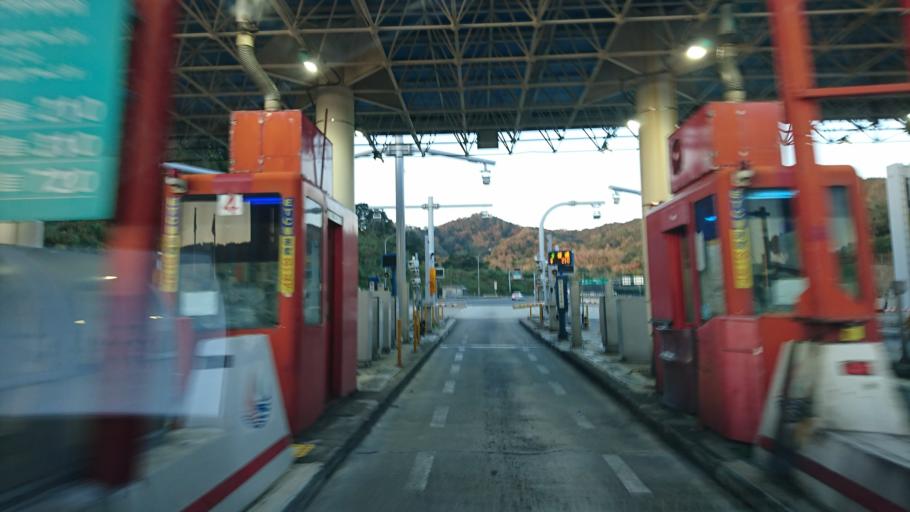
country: JP
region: Hyogo
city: Kobe
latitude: 34.6507
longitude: 135.1067
